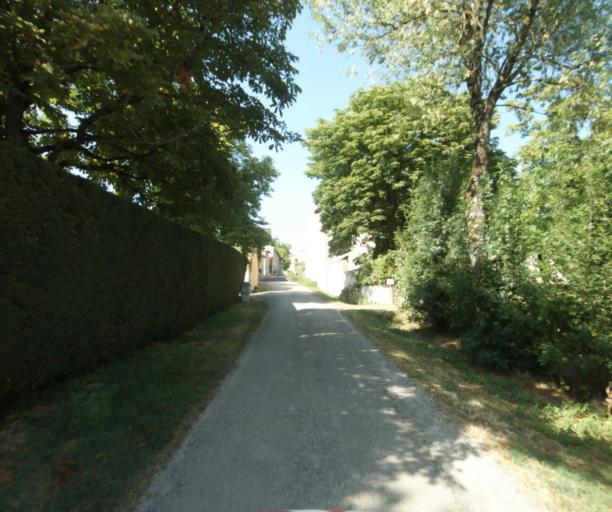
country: FR
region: Midi-Pyrenees
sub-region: Departement du Tarn
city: Puylaurens
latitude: 43.5200
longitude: 1.9850
